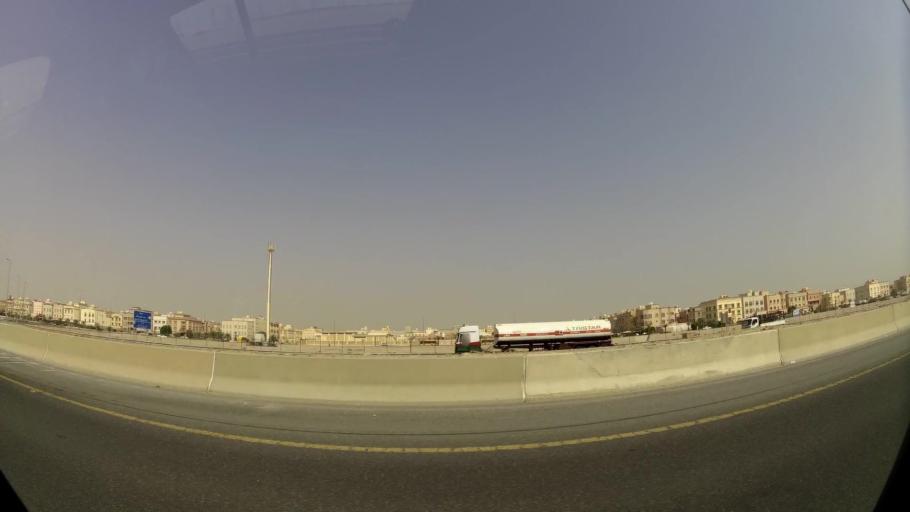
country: KW
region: Muhafazat al Jahra'
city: Al Jahra'
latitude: 29.2996
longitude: 47.7051
